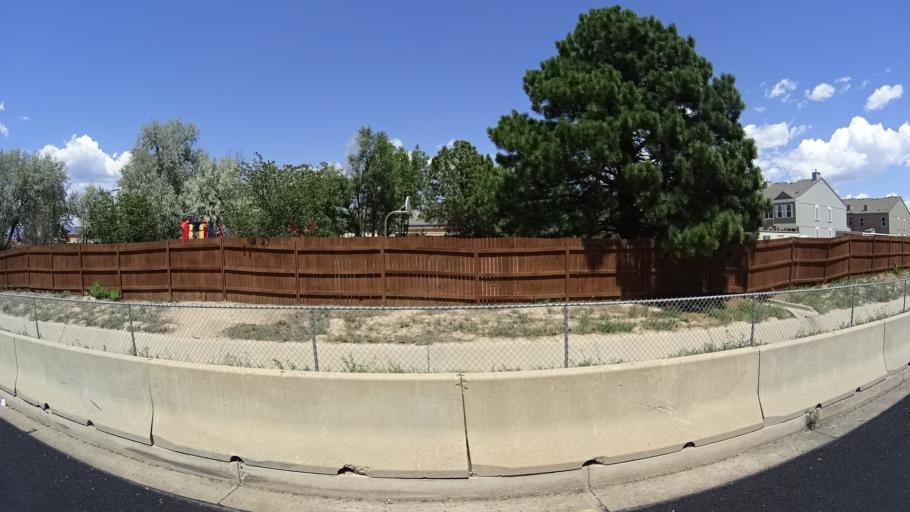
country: US
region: Colorado
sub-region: El Paso County
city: Stratmoor
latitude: 38.7891
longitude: -104.7525
